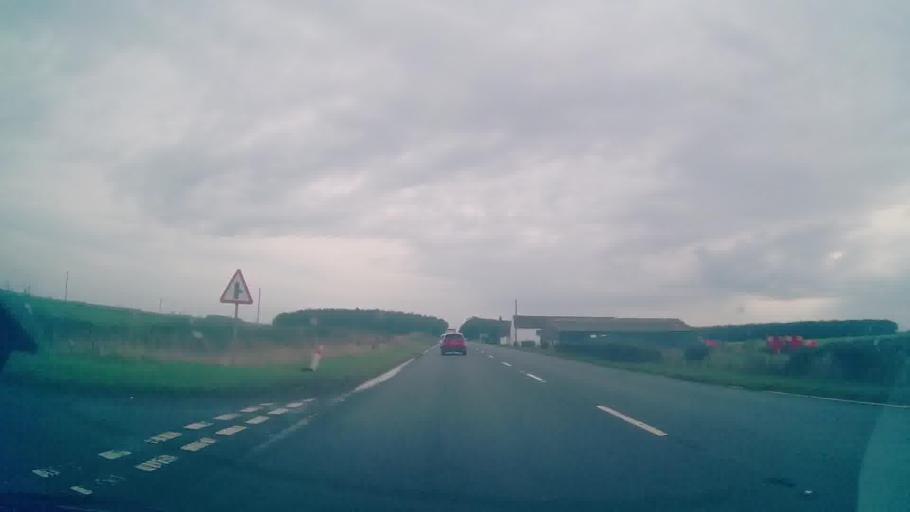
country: GB
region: Scotland
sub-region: Dumfries and Galloway
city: Annan
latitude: 55.0037
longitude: -3.3161
